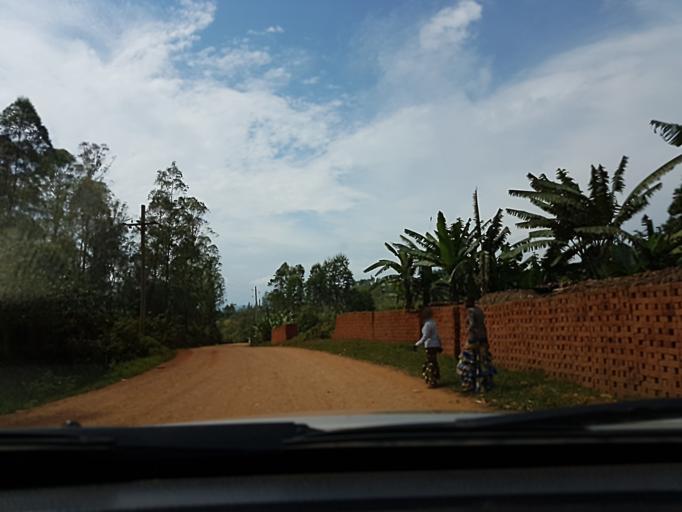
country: CD
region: South Kivu
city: Bukavu
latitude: -2.6504
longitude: 28.8732
